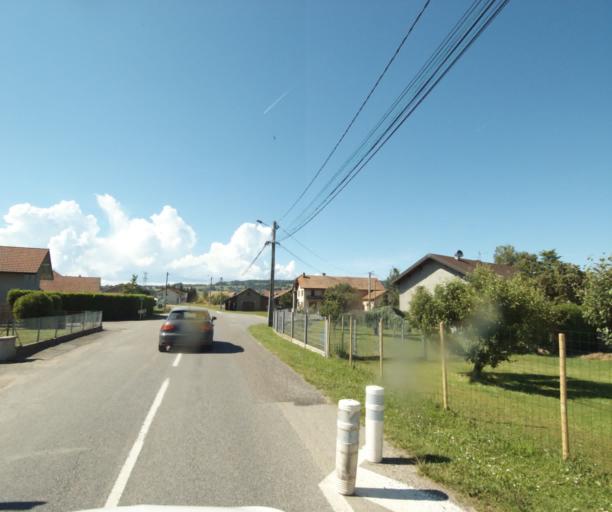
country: FR
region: Rhone-Alpes
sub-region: Departement de la Haute-Savoie
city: Bons-en-Chablais
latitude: 46.2765
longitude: 6.3606
